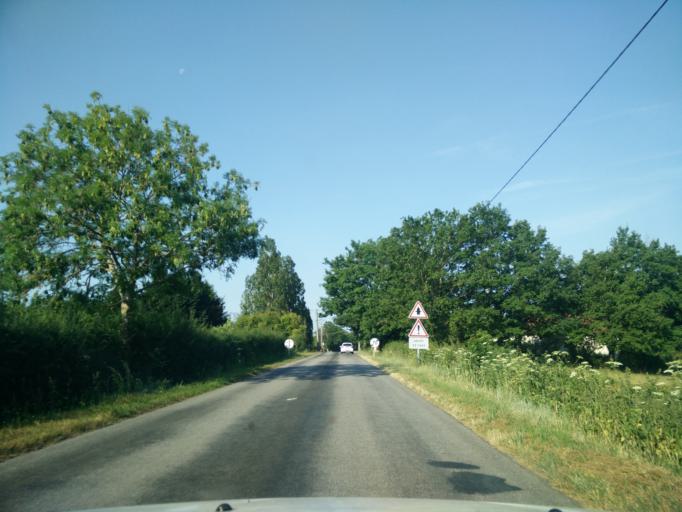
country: FR
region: Auvergne
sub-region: Departement de l'Allier
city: Toulon-sur-Allier
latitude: 46.4829
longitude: 3.3052
